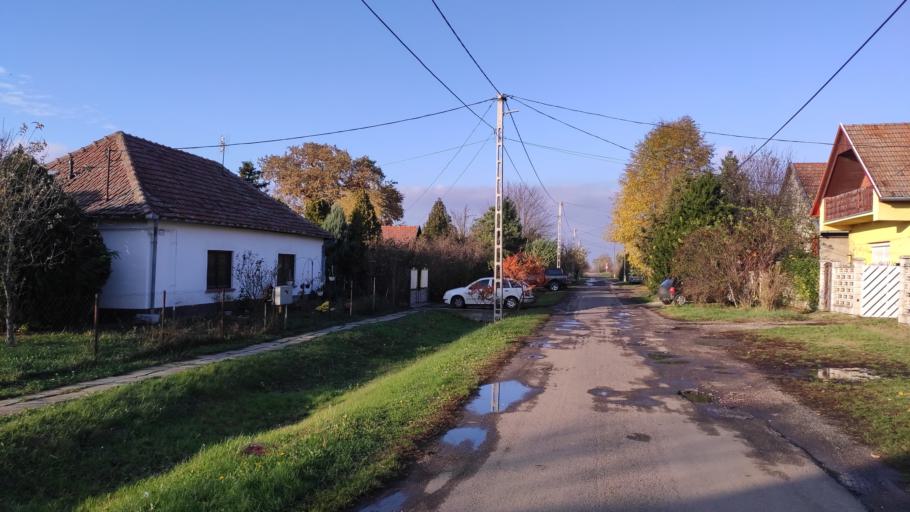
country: HU
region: Bekes
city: Mezobereny
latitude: 46.7629
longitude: 21.0448
